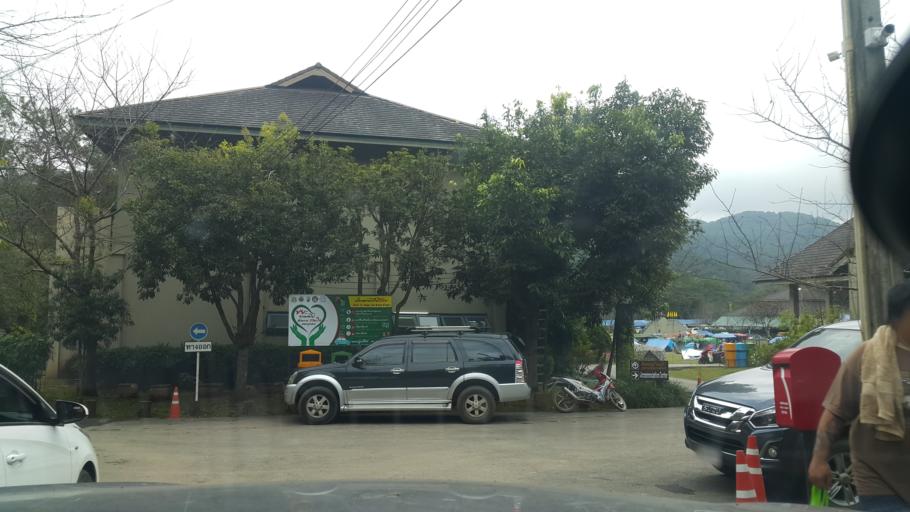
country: TH
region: Chiang Mai
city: Mae Chaem
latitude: 18.5369
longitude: 98.5219
